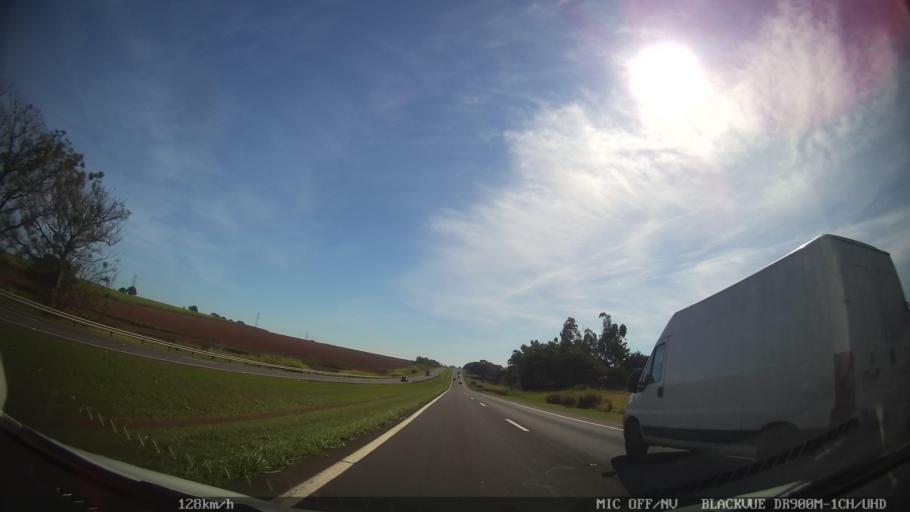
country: BR
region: Sao Paulo
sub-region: Leme
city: Leme
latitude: -22.1309
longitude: -47.4096
